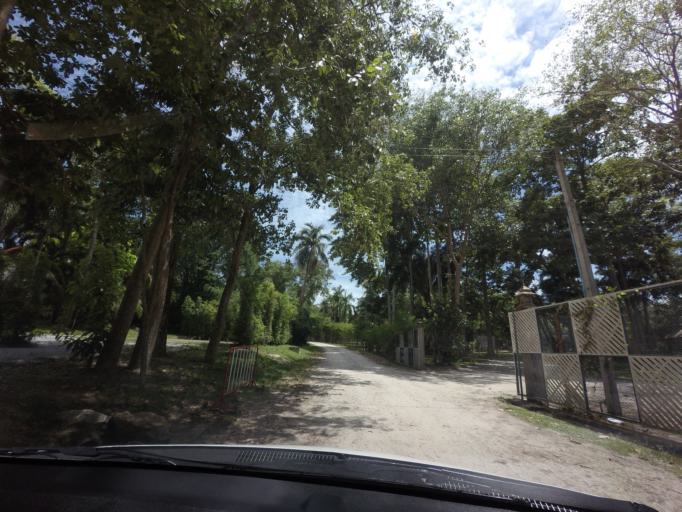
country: TH
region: Chon Buri
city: Sattahip
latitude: 12.7476
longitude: 100.9143
